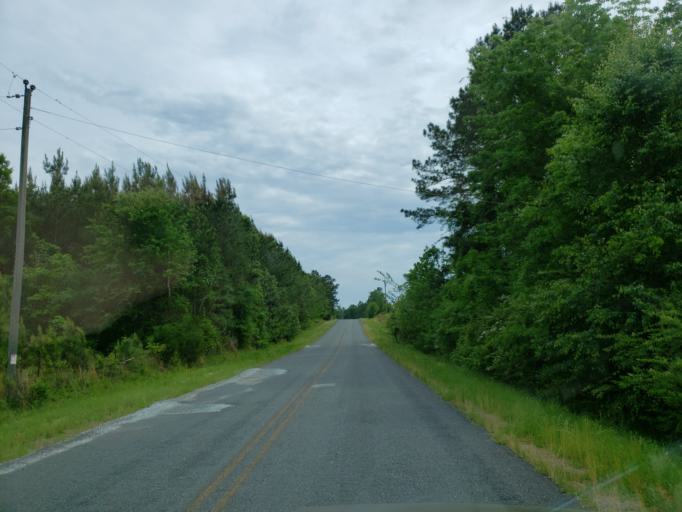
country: US
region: Georgia
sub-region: Bibb County
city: West Point
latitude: 32.8585
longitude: -83.8918
